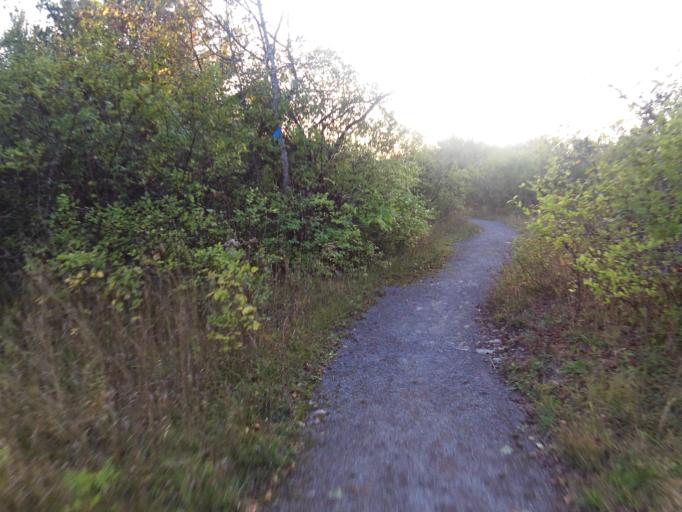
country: CA
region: Ontario
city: Bells Corners
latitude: 45.3705
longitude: -75.7901
